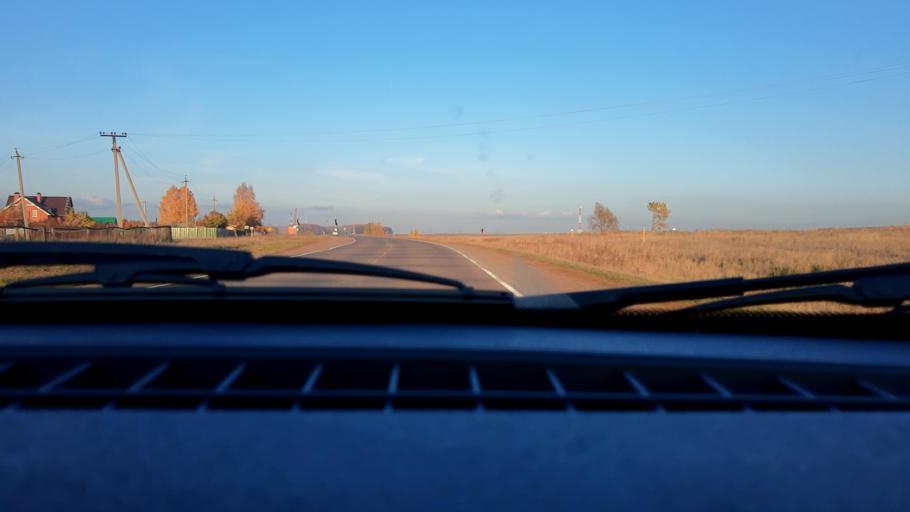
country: RU
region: Bashkortostan
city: Asanovo
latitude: 54.8065
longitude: 55.5652
